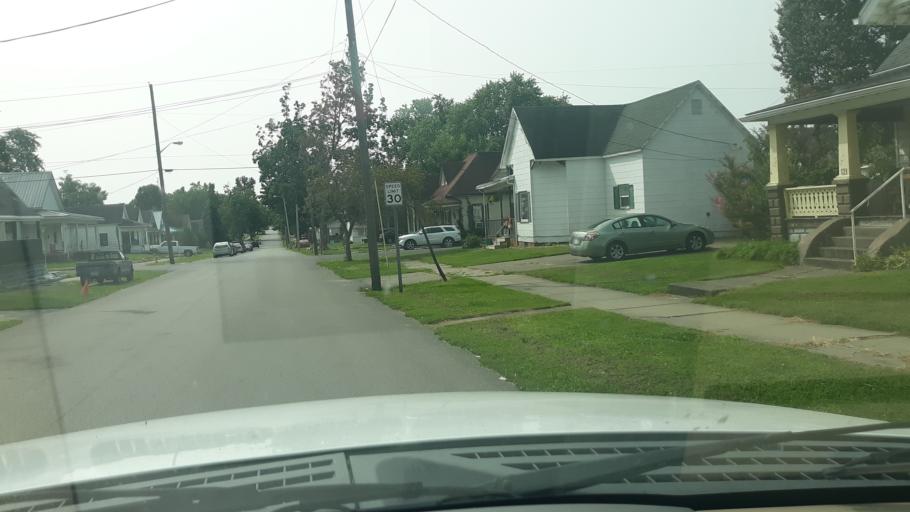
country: US
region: Indiana
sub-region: Gibson County
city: Princeton
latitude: 38.3548
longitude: -87.5638
